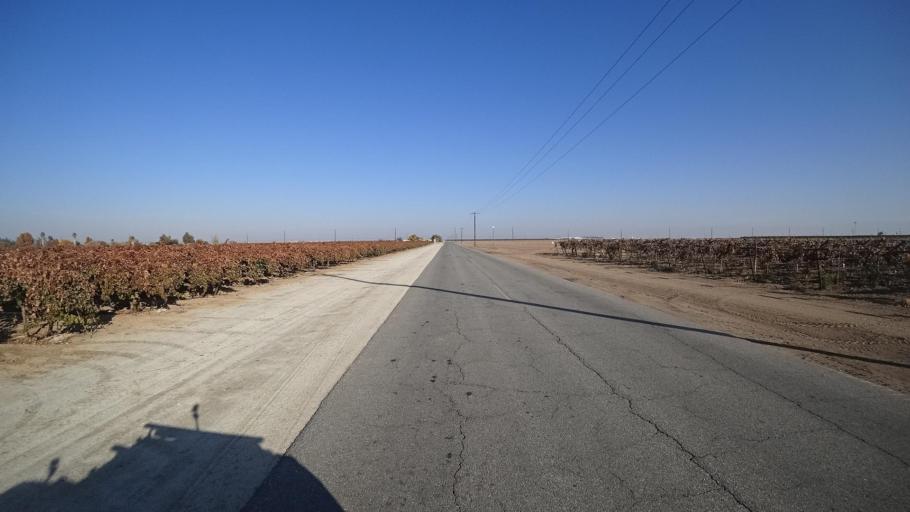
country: US
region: California
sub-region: Tulare County
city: Richgrove
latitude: 35.7720
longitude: -119.1697
